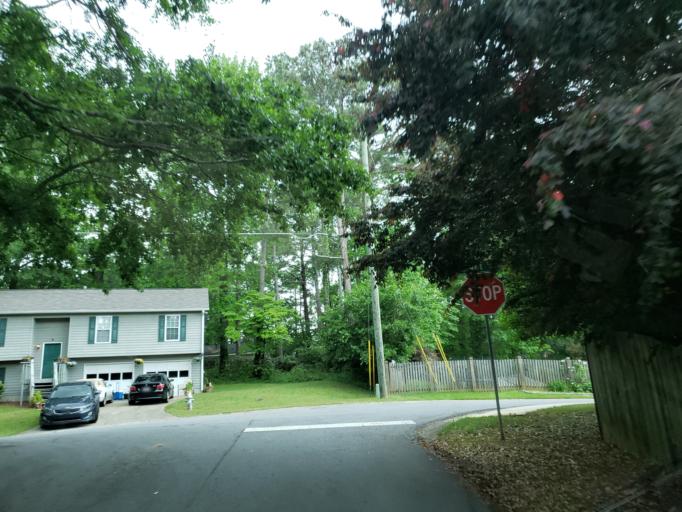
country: US
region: Georgia
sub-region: Cobb County
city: Marietta
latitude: 33.9586
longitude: -84.5725
